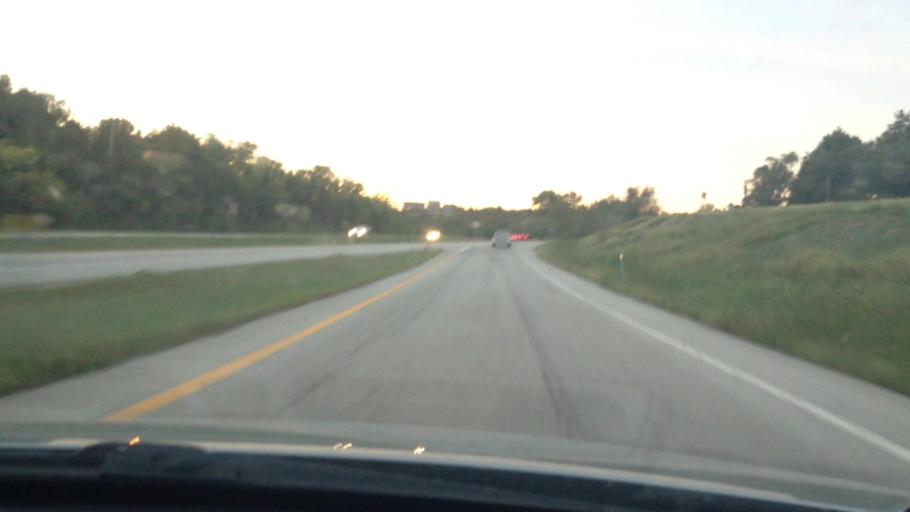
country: US
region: Missouri
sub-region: Jackson County
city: Lees Summit
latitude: 38.9457
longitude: -94.4090
